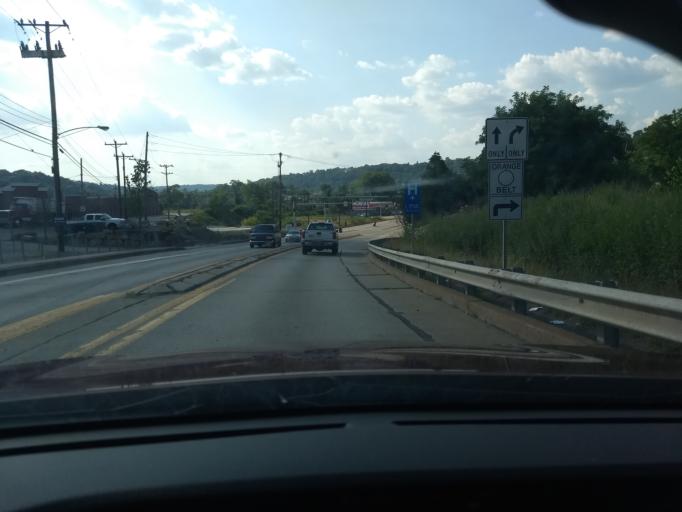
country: US
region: Pennsylvania
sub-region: Allegheny County
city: Versailles
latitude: 40.3227
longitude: -79.8382
